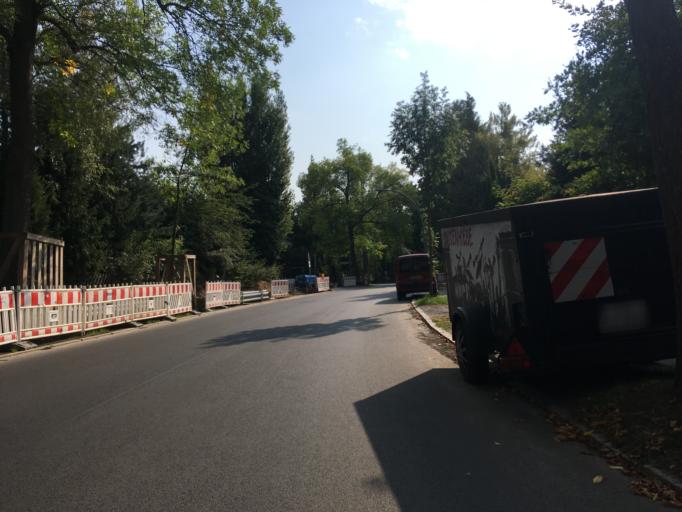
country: DE
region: Berlin
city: Frohnau
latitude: 52.6320
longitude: 13.2811
